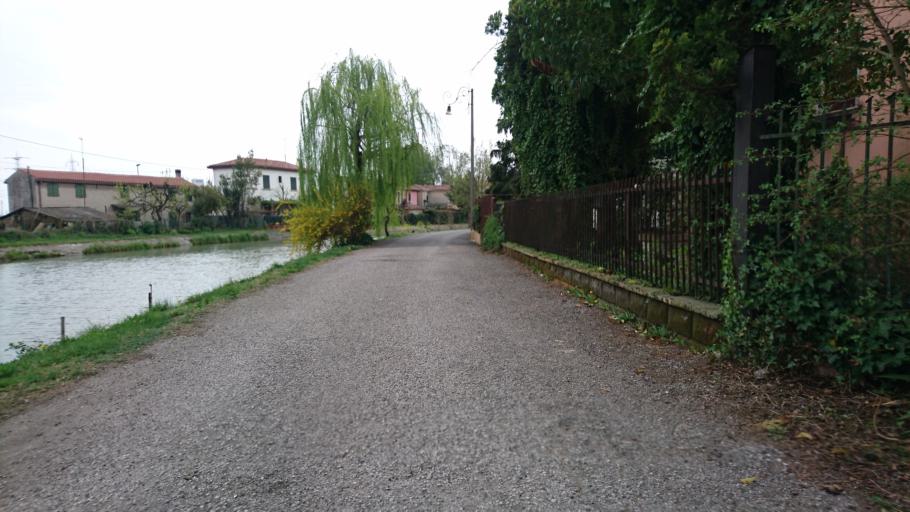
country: IT
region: Veneto
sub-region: Provincia di Venezia
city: Mestre
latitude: 45.4355
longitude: 12.2070
